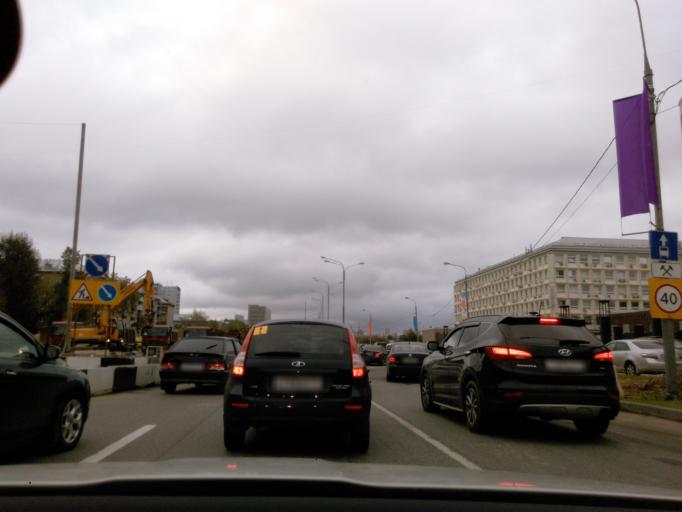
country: RU
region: Moscow
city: Strogino
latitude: 55.8261
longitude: 37.4275
